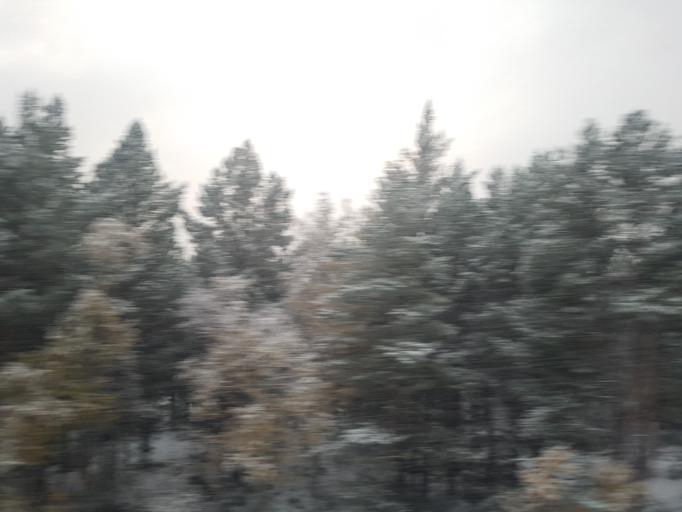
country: NO
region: Oppland
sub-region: Dovre
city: Dombas
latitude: 62.0890
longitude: 9.0985
